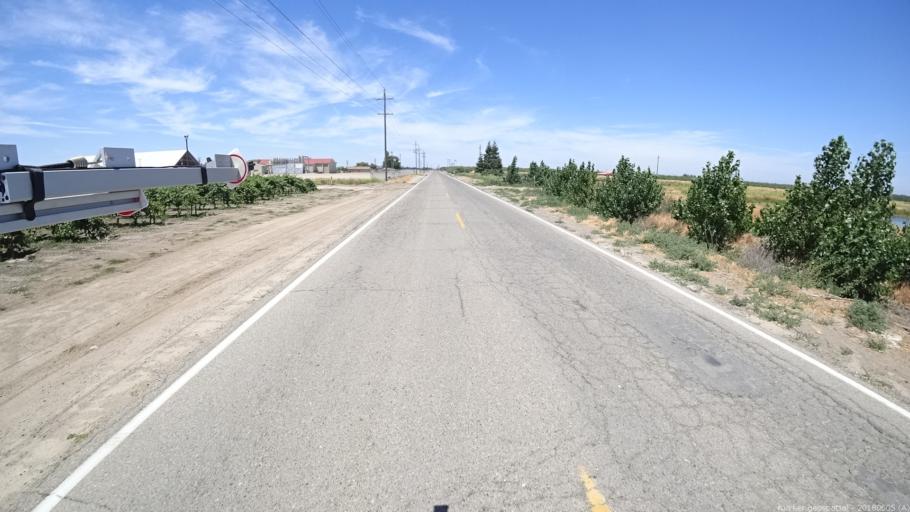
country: US
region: California
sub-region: Merced County
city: Dos Palos
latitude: 37.0786
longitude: -120.4735
